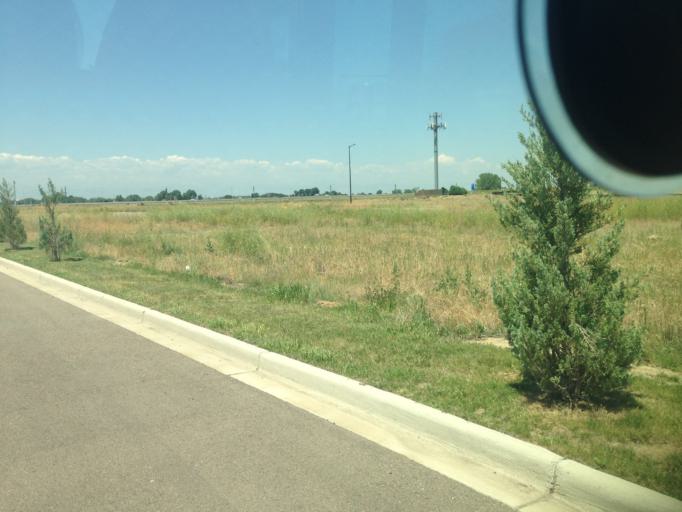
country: US
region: Colorado
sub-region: Adams County
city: Aurora
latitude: 39.8097
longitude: -104.7801
